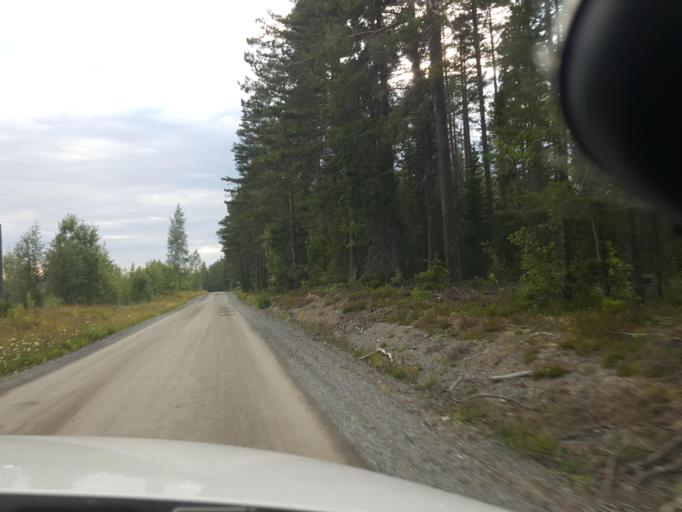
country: SE
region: Vaesternorrland
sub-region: Ange Kommun
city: Ange
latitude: 62.3045
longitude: 15.7256
